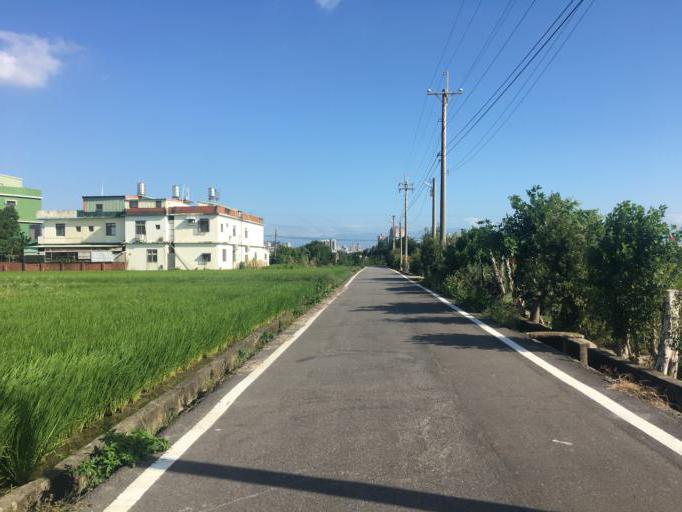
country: TW
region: Taiwan
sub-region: Hsinchu
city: Zhubei
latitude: 24.8382
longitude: 120.9903
